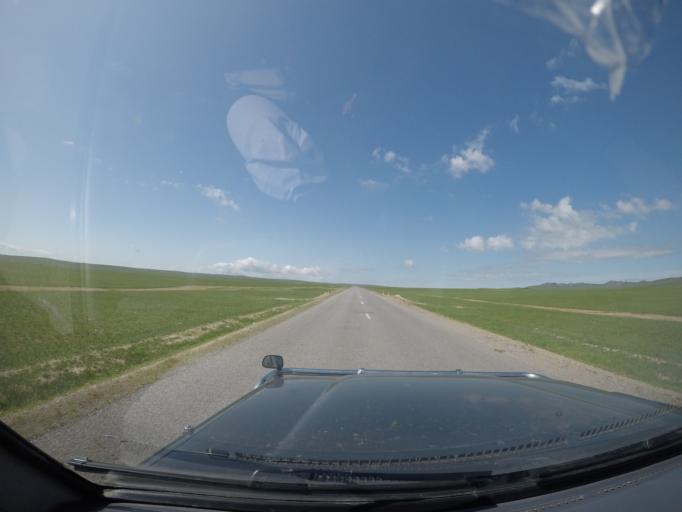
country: MN
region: Hentiy
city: Bayan
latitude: 47.3209
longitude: 111.4110
